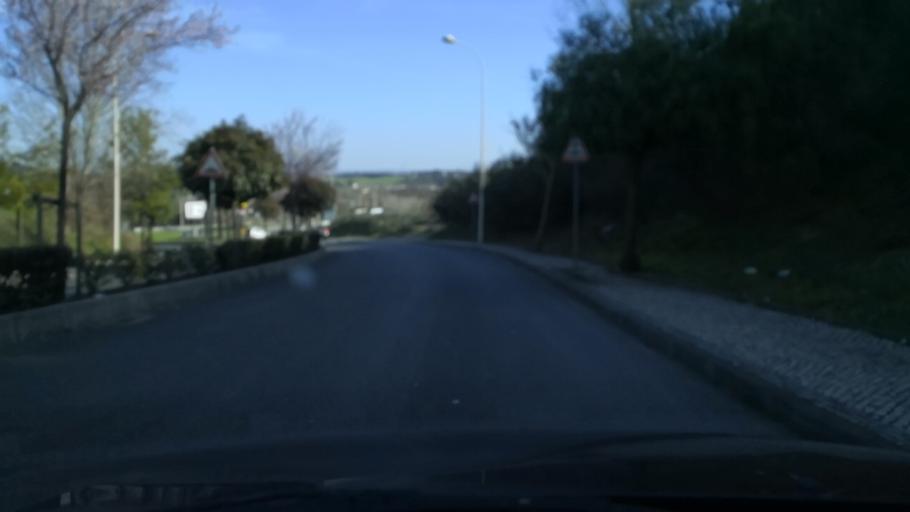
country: PT
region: Santarem
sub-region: Torres Novas
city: Torres Novas
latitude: 39.4692
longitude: -8.5354
